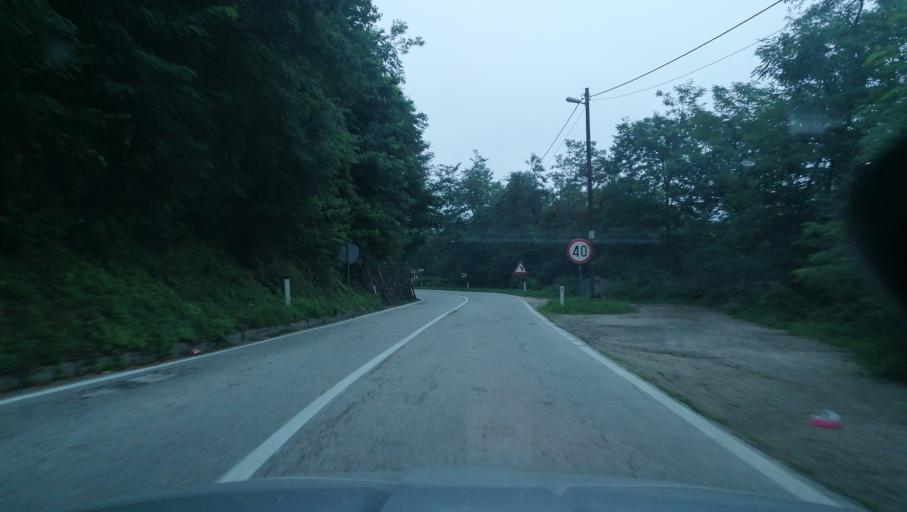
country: BA
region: Federation of Bosnia and Herzegovina
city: Jablanica
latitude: 43.7105
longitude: 17.7128
